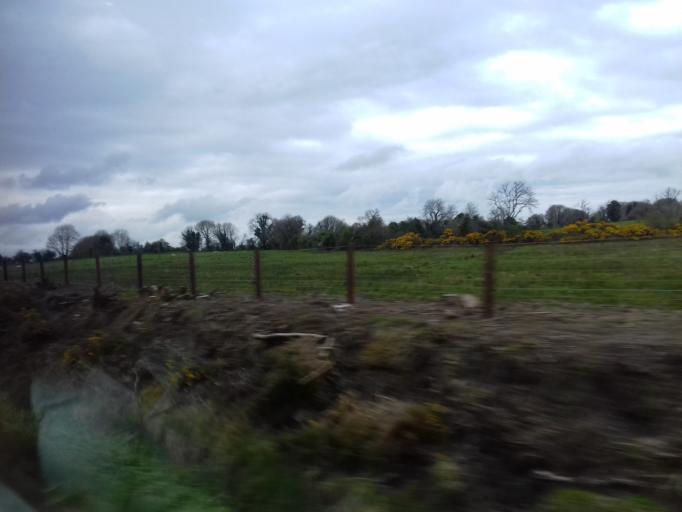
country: IE
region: Leinster
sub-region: An Longfort
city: Edgeworthstown
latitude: 53.6976
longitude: -7.6495
